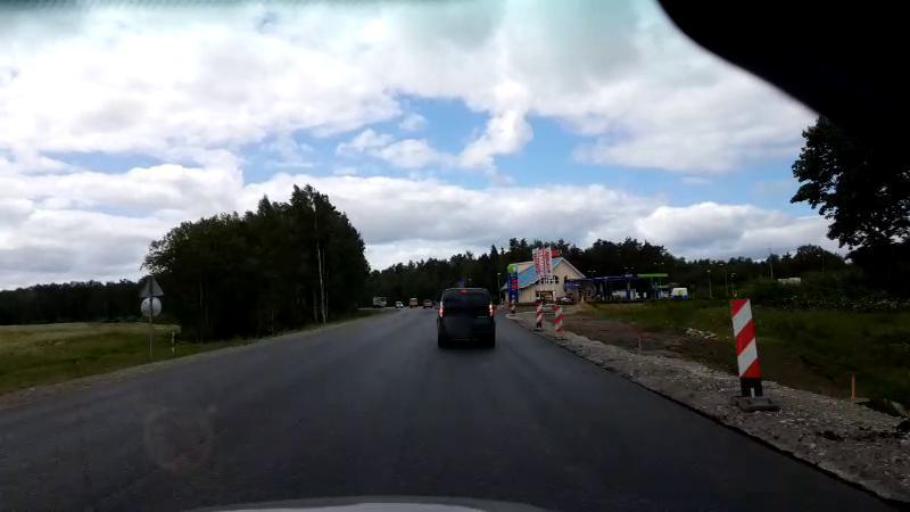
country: LV
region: Salacgrivas
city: Ainazi
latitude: 57.8479
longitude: 24.3523
